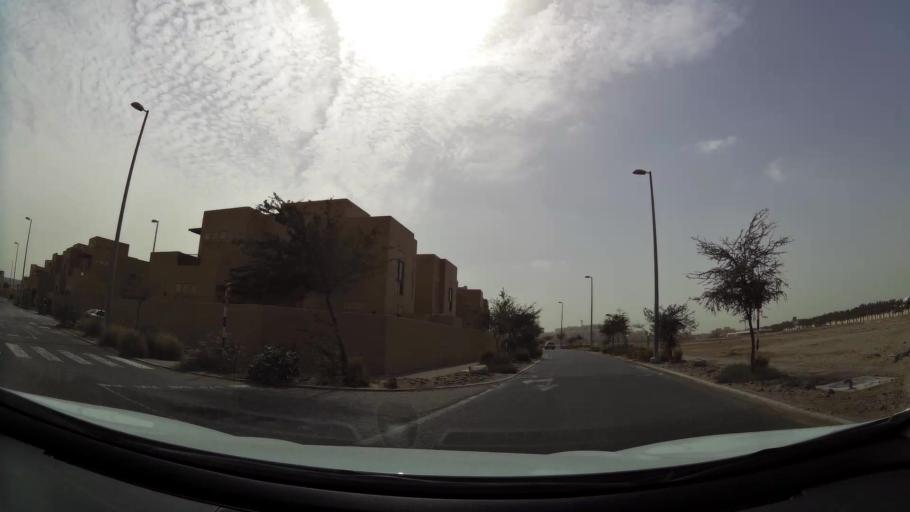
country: AE
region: Abu Dhabi
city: Abu Dhabi
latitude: 24.4174
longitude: 54.5455
